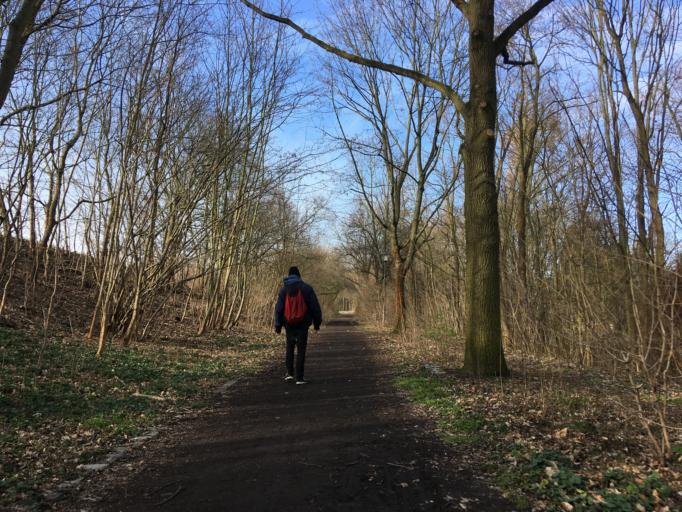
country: DE
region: Berlin
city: Rosenthal
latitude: 52.6115
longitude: 13.3723
